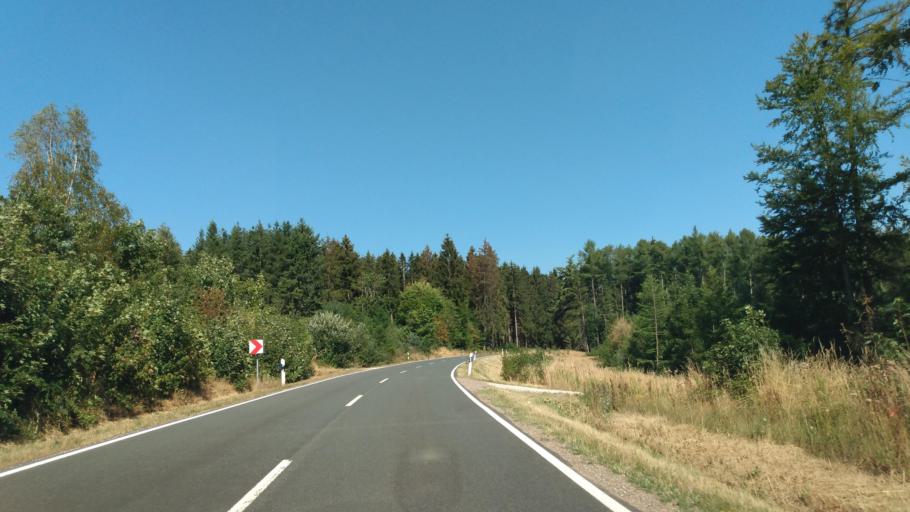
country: DE
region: Rheinland-Pfalz
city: Lotzbeuren
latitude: 49.9107
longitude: 7.2069
